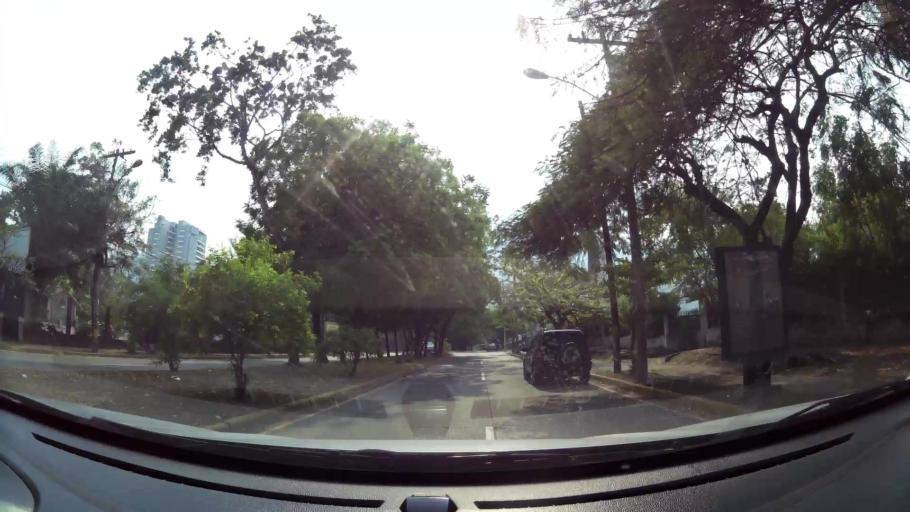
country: HN
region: Cortes
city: Armenta
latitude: 15.5075
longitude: -88.0435
